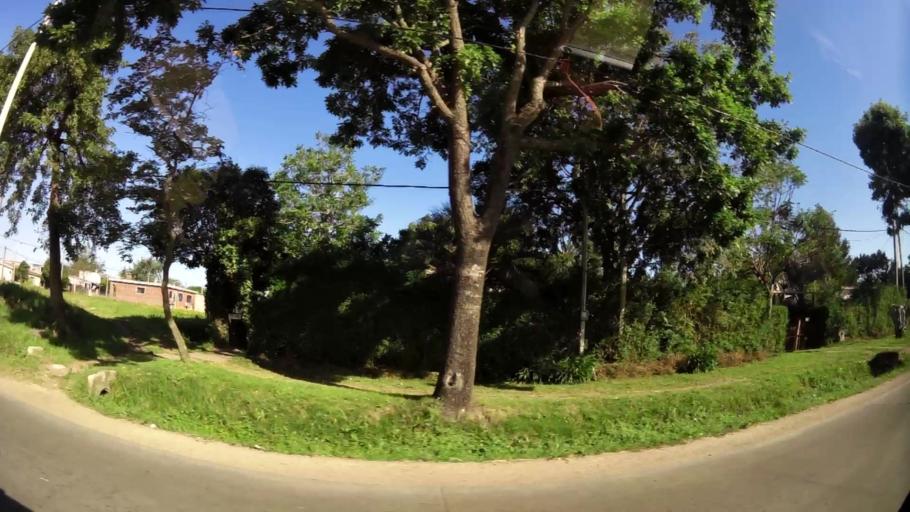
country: UY
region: Canelones
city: La Paz
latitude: -34.8183
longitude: -56.1741
